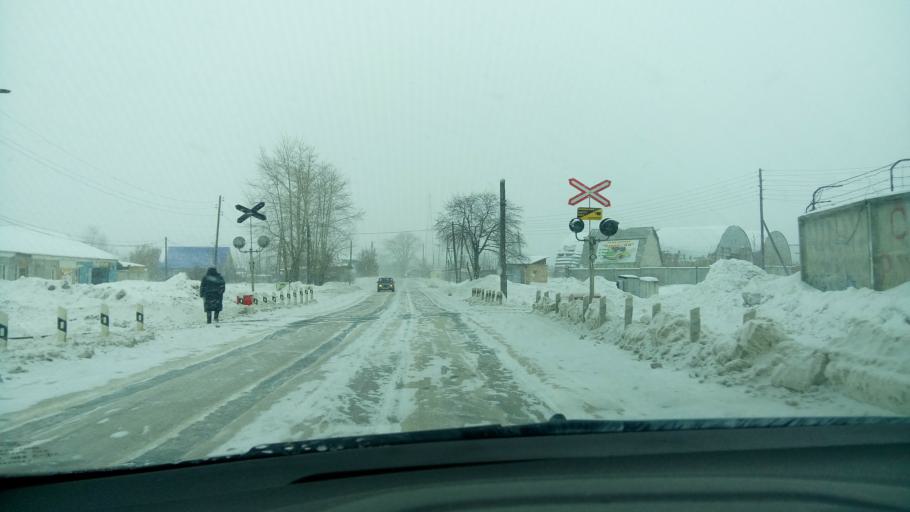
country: RU
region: Sverdlovsk
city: Bogdanovich
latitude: 56.7805
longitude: 62.0292
